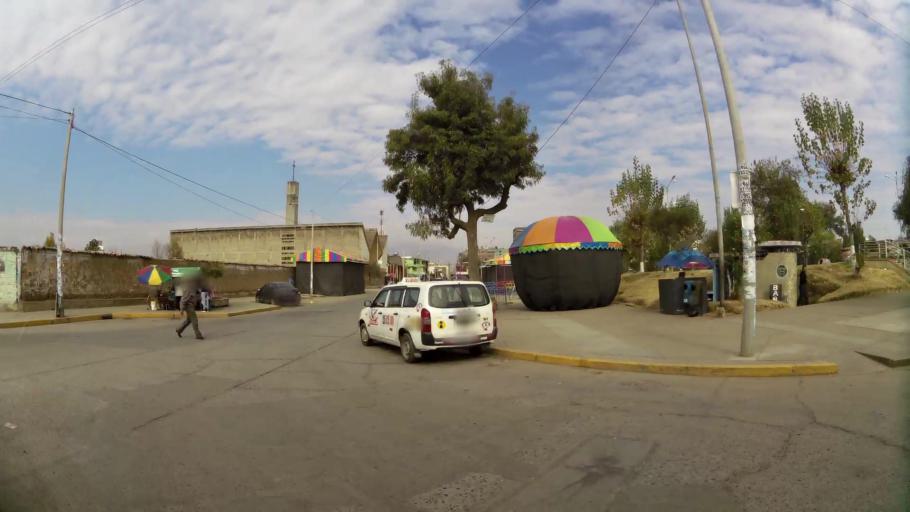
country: PE
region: Junin
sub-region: Provincia de Huancayo
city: Huancayo
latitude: -12.0603
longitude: -75.2030
